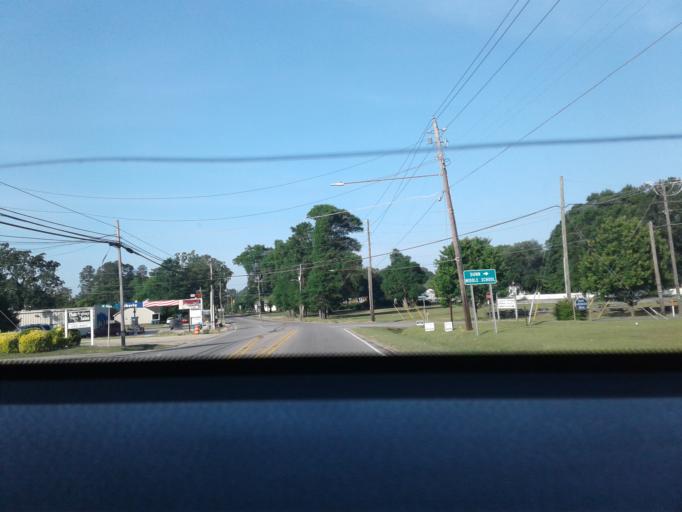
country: US
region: North Carolina
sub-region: Harnett County
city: Dunn
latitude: 35.3204
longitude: -78.6075
